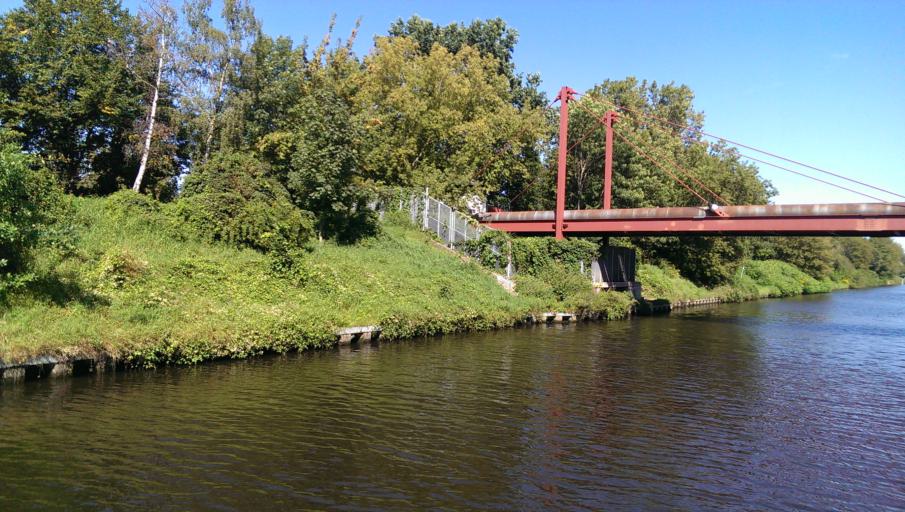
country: DE
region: Berlin
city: Lichterfelde
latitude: 52.4253
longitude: 13.3068
